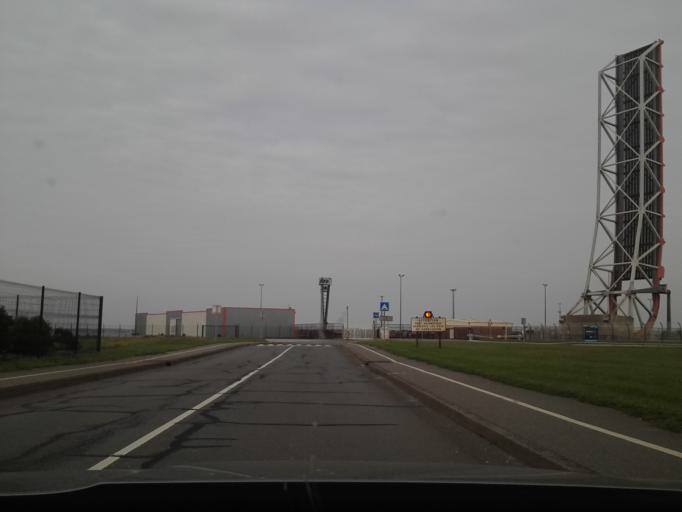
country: FR
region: Nord-Pas-de-Calais
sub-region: Departement du Nord
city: Saint-Pol-sur-Mer
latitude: 51.0536
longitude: 2.3408
